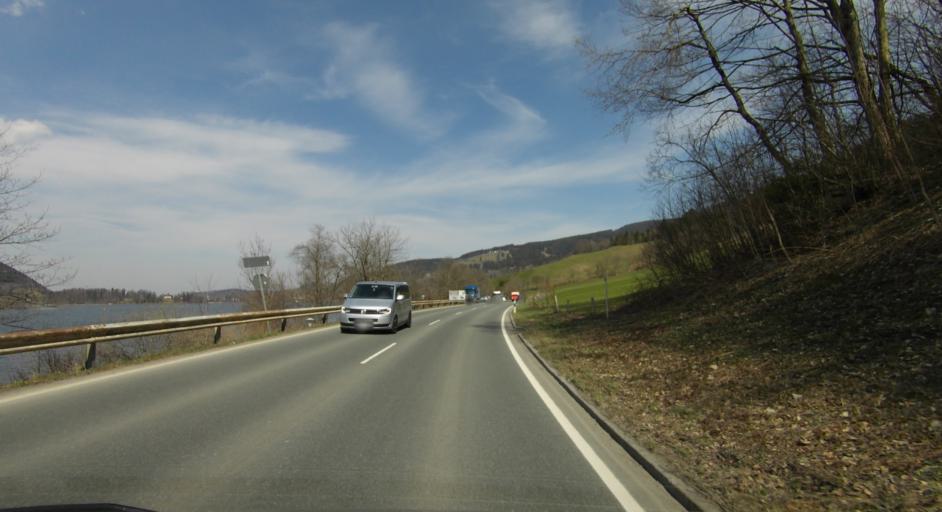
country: DE
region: Bavaria
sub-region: Upper Bavaria
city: Schliersee
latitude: 47.7165
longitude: 11.8694
